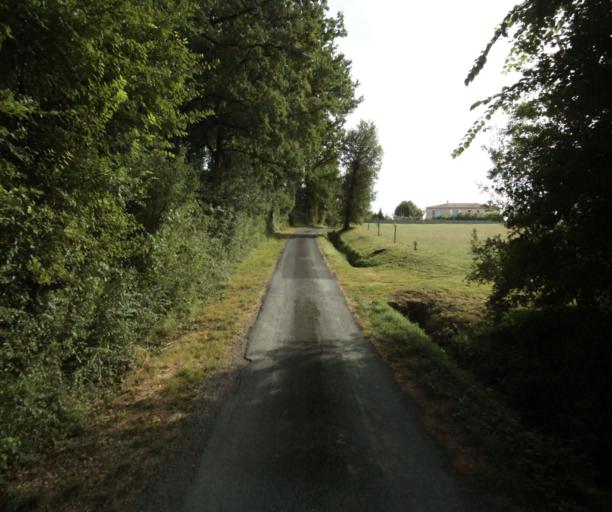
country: FR
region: Midi-Pyrenees
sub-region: Departement du Tarn
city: Soual
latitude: 43.5433
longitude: 2.0646
